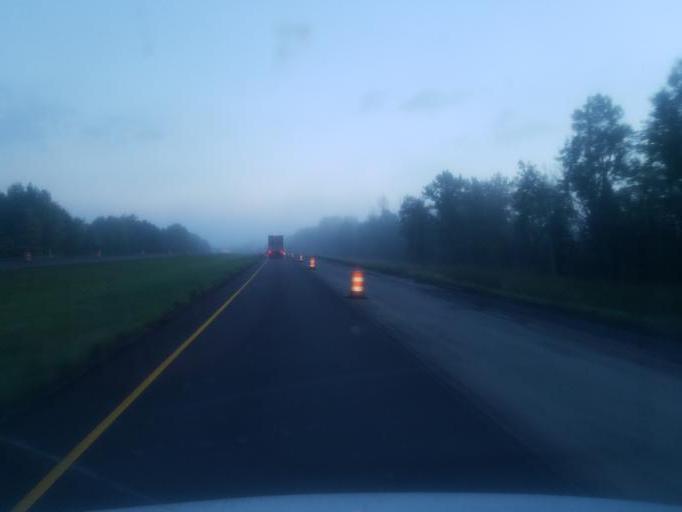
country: US
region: Ohio
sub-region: Ashtabula County
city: Jefferson
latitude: 41.7165
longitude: -80.7074
